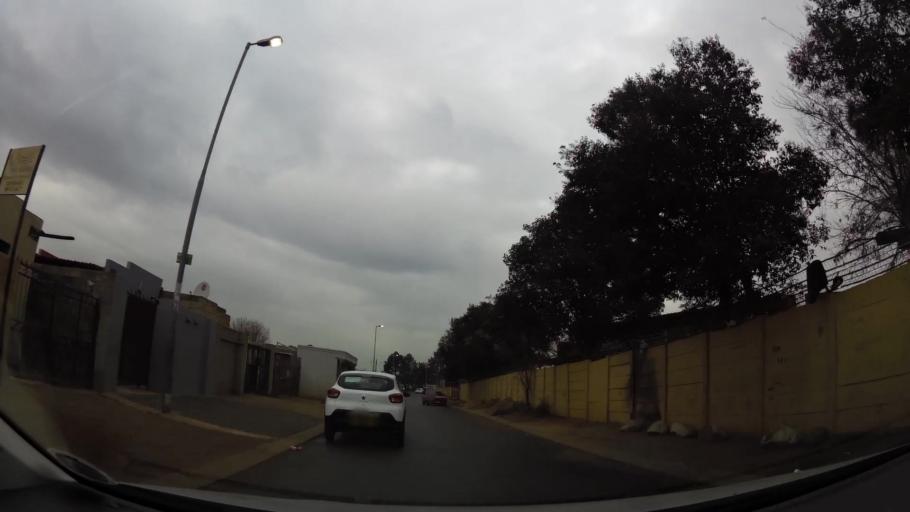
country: ZA
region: Gauteng
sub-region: City of Johannesburg Metropolitan Municipality
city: Soweto
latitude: -26.2501
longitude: 27.8762
